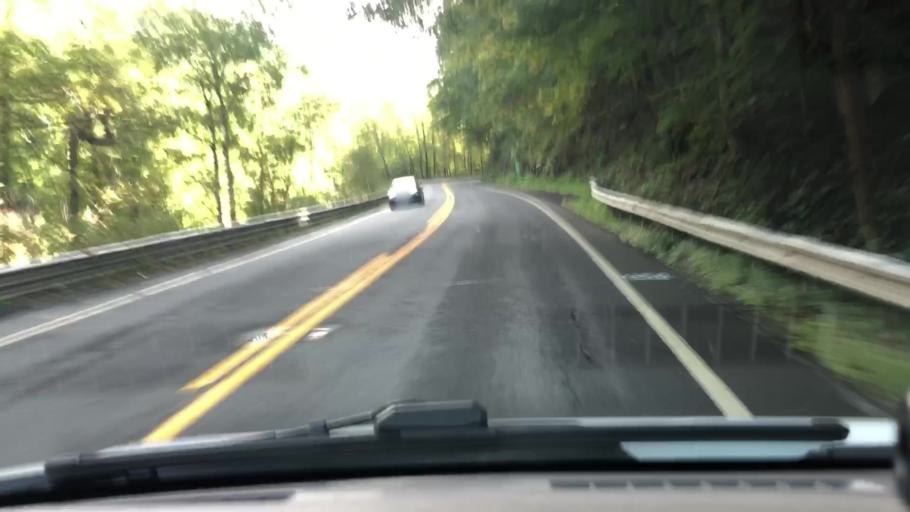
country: US
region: Massachusetts
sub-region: Franklin County
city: Charlemont
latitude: 42.6411
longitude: -72.9574
